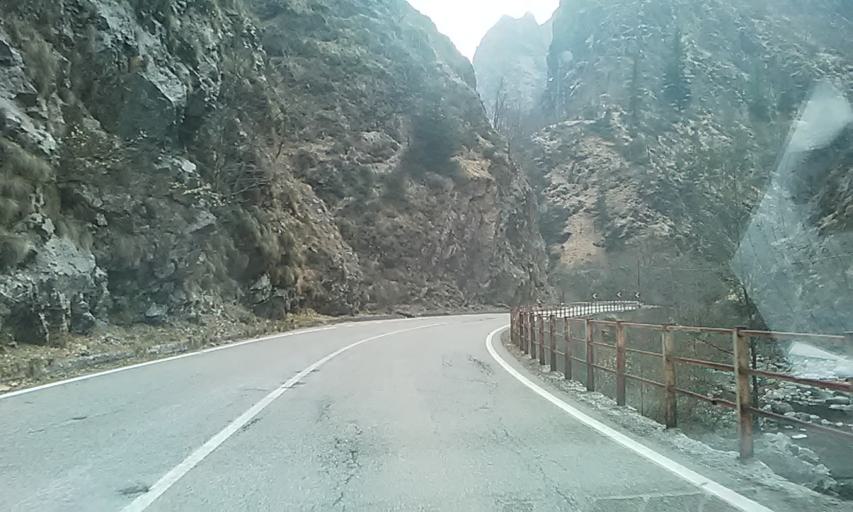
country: IT
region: Piedmont
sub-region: Provincia di Vercelli
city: Cervatto
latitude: 45.8847
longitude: 8.1664
